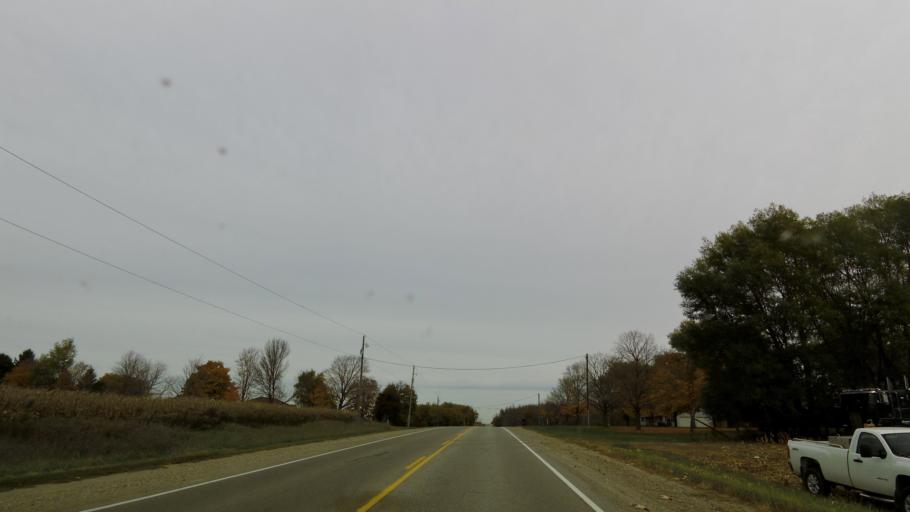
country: CA
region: Ontario
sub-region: Wellington County
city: Guelph
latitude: 43.5104
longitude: -80.3045
